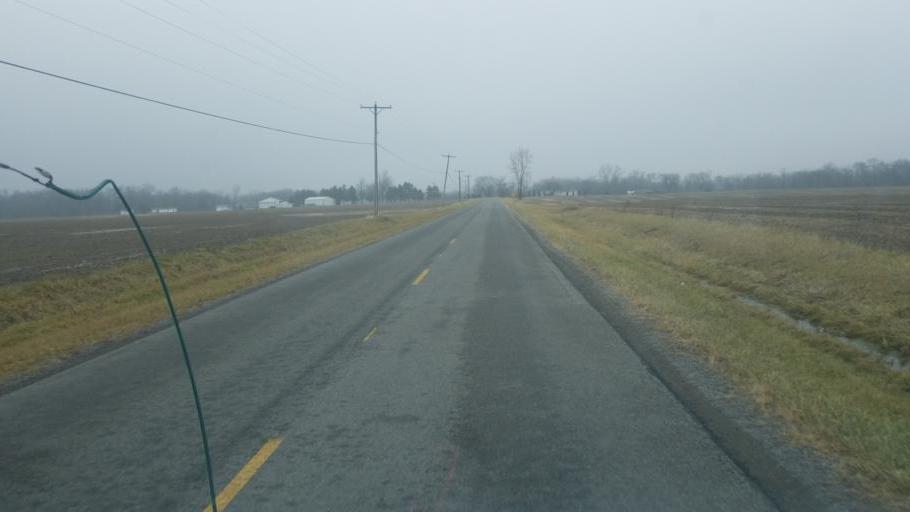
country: US
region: Ohio
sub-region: Champaign County
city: North Lewisburg
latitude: 40.3470
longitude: -83.5571
